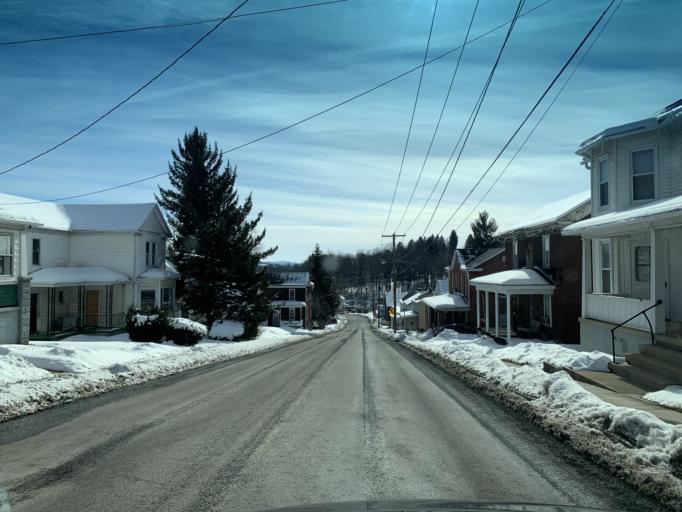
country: US
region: Maryland
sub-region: Allegany County
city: Frostburg
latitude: 39.6530
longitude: -78.9223
